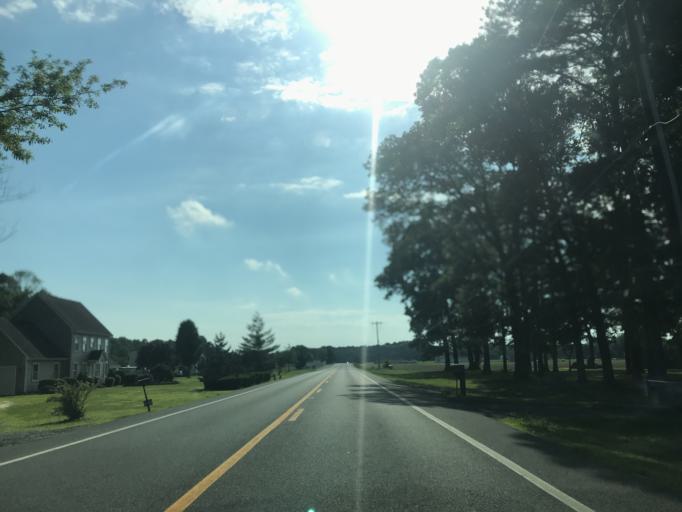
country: US
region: Maryland
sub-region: Wicomico County
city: Hebron
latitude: 38.4658
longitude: -75.7145
